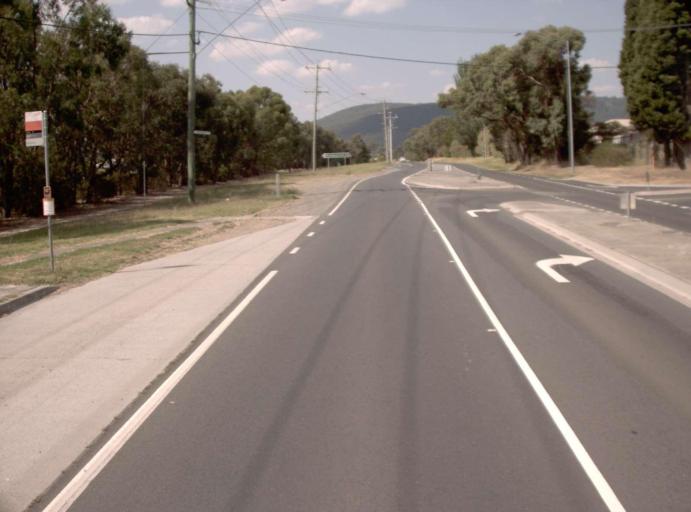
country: AU
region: Victoria
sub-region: Knox
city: Ferntree Gully
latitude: -37.9063
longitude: 145.2801
